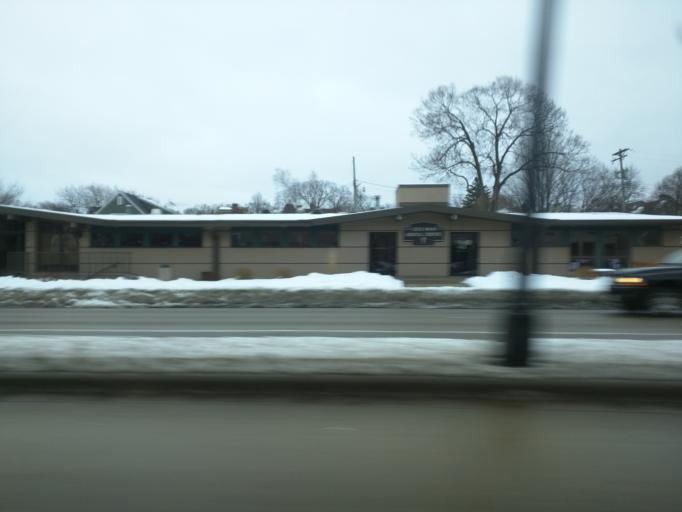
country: US
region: Wisconsin
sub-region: La Crosse County
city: La Crosse
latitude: 43.8113
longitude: -91.2390
